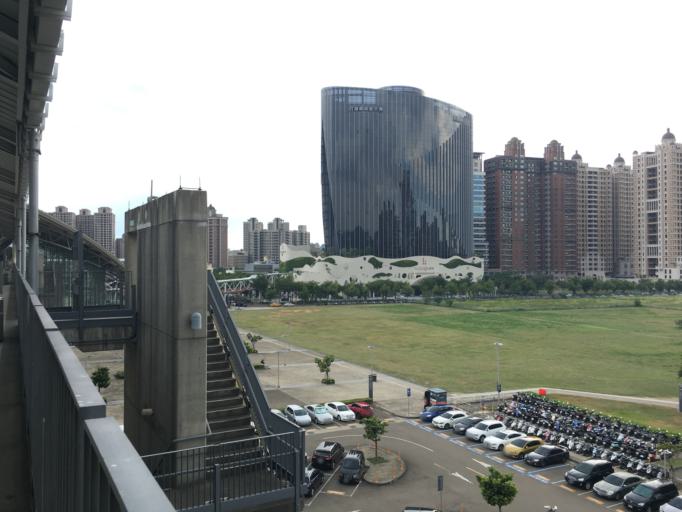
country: TW
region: Taiwan
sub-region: Hsinchu
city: Zhubei
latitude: 24.8094
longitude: 121.0404
